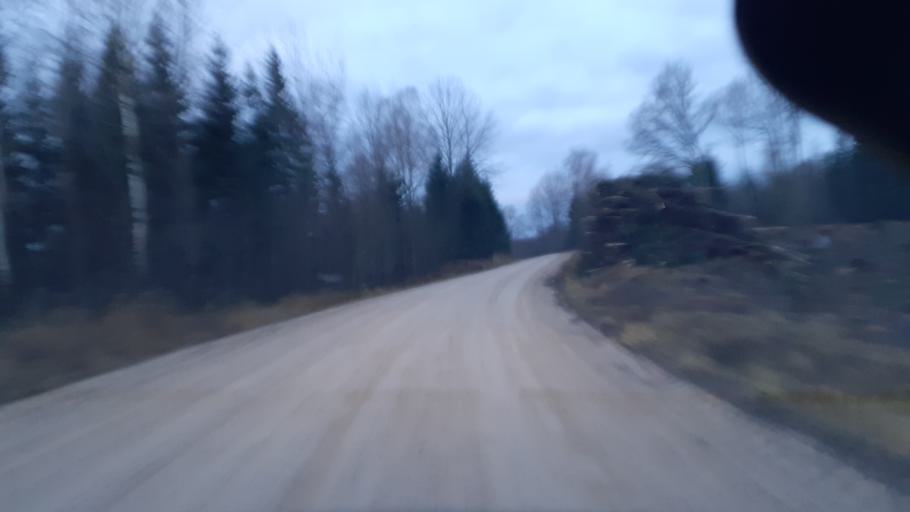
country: LV
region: Kuldigas Rajons
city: Kuldiga
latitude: 56.9538
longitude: 21.7933
